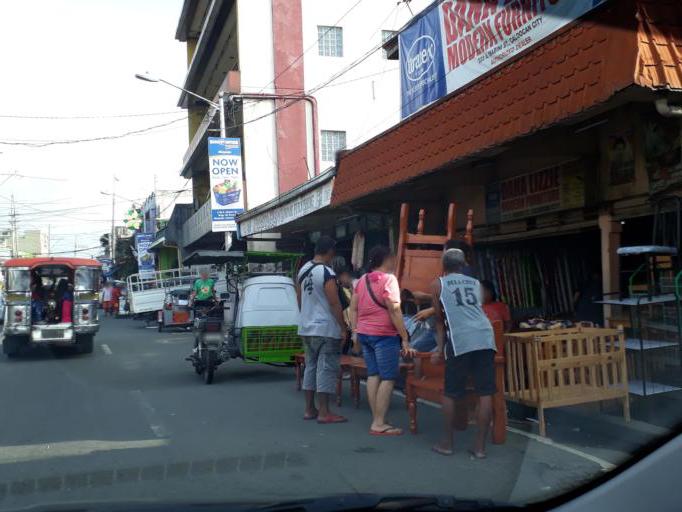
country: PH
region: Metro Manila
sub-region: Caloocan City
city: Niugan
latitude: 14.6449
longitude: 120.9753
